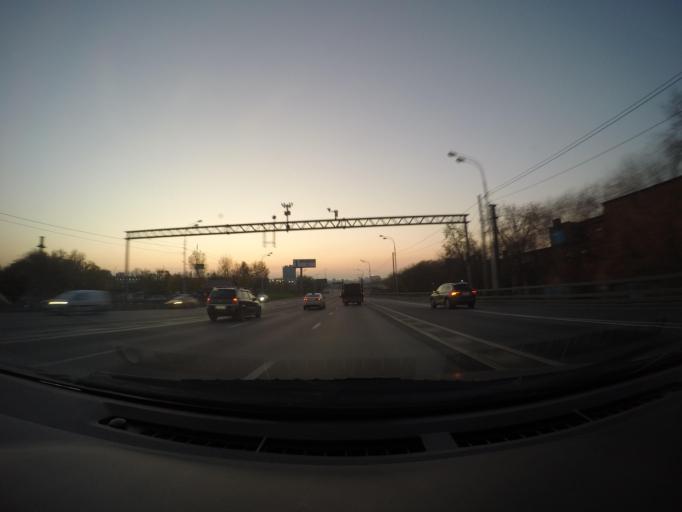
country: RU
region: Moscow
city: Taganskiy
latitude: 55.7183
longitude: 37.7049
